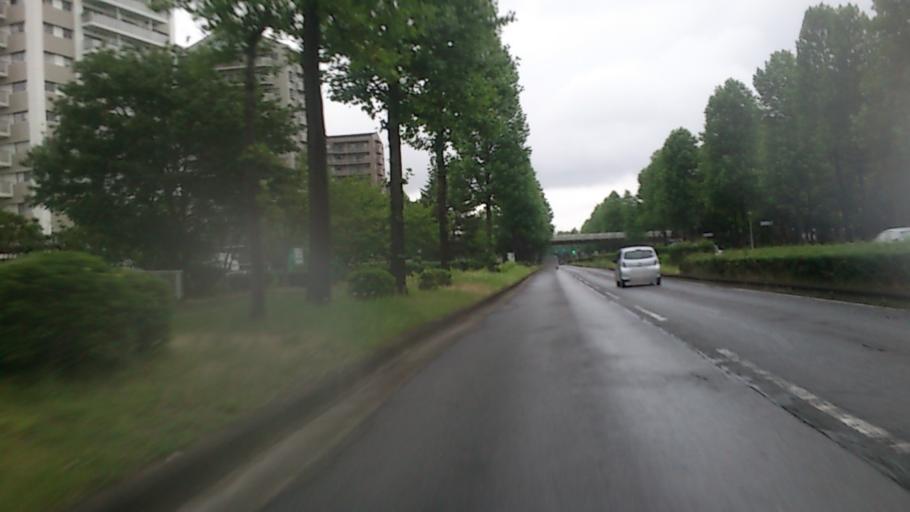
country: JP
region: Ibaraki
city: Naka
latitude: 36.0586
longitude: 140.1203
